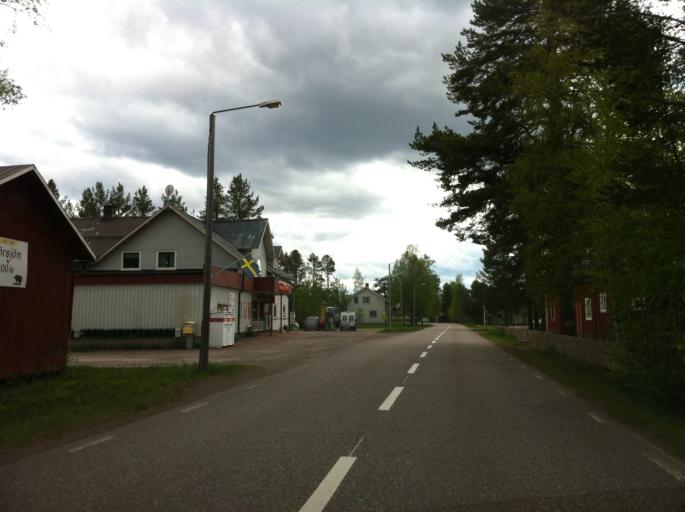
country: NO
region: Hedmark
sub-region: Trysil
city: Innbygda
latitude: 61.4112
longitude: 13.0838
